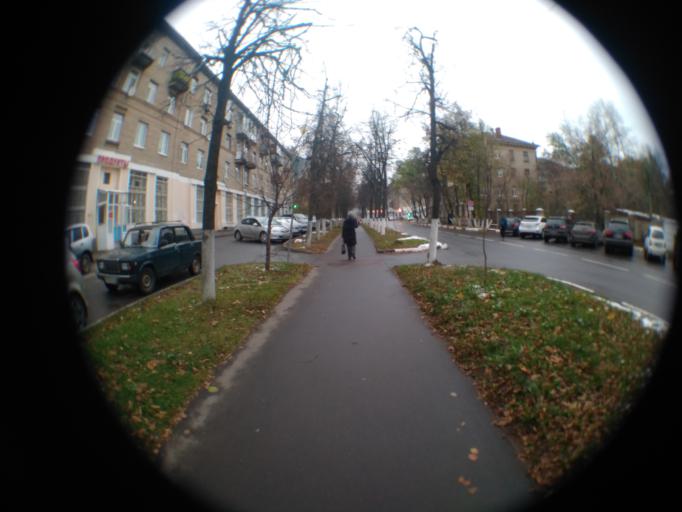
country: RU
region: Moskovskaya
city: Zhukovskiy
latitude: 55.5908
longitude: 38.1285
